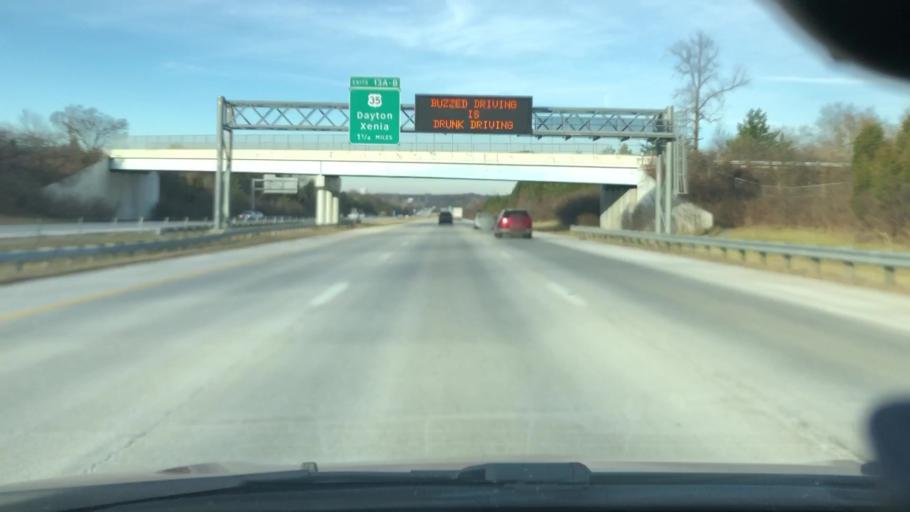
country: US
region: Ohio
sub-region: Greene County
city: Beavercreek
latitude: 39.7143
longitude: -84.0917
